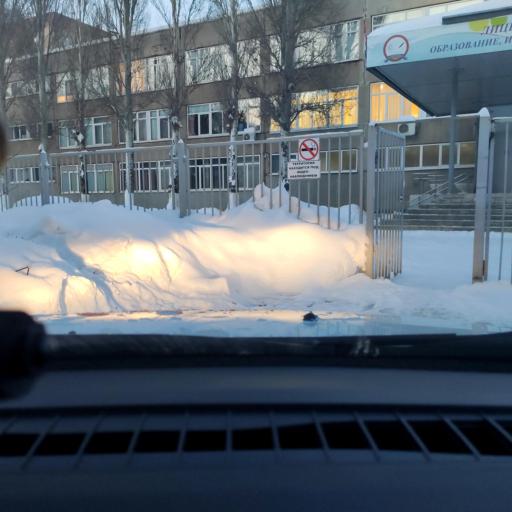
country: RU
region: Samara
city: Samara
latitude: 53.1999
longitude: 50.2281
